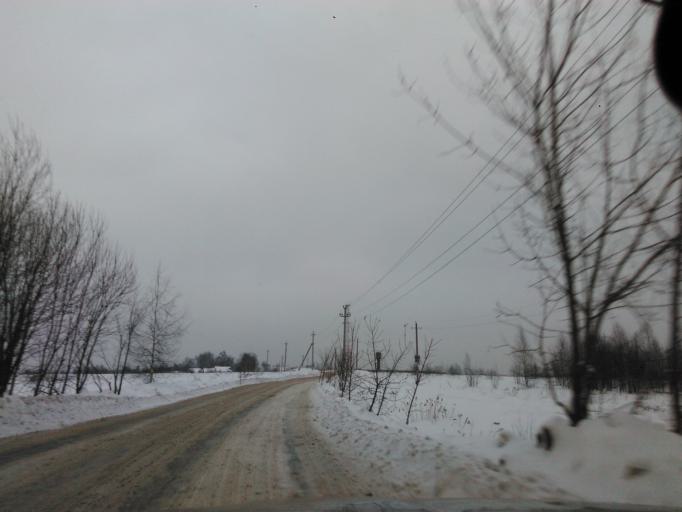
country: RU
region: Moskovskaya
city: Yakhroma
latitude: 56.2651
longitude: 37.4420
